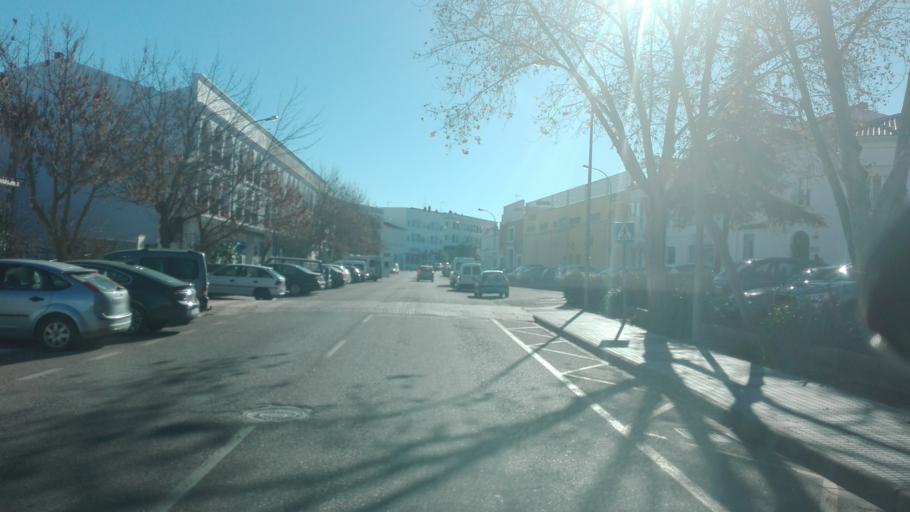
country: ES
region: Extremadura
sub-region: Provincia de Badajoz
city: Llerena
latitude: 38.2402
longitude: -6.0142
